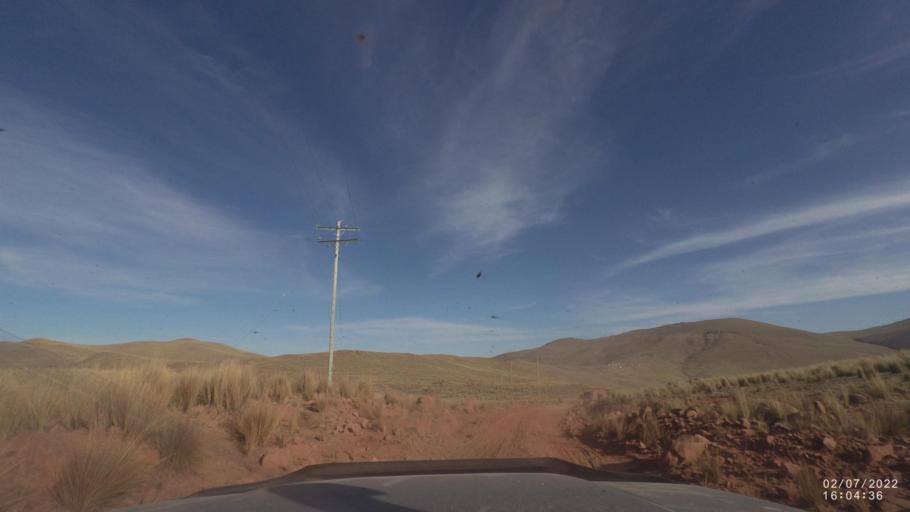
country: BO
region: Cochabamba
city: Irpa Irpa
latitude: -17.9127
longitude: -66.4400
